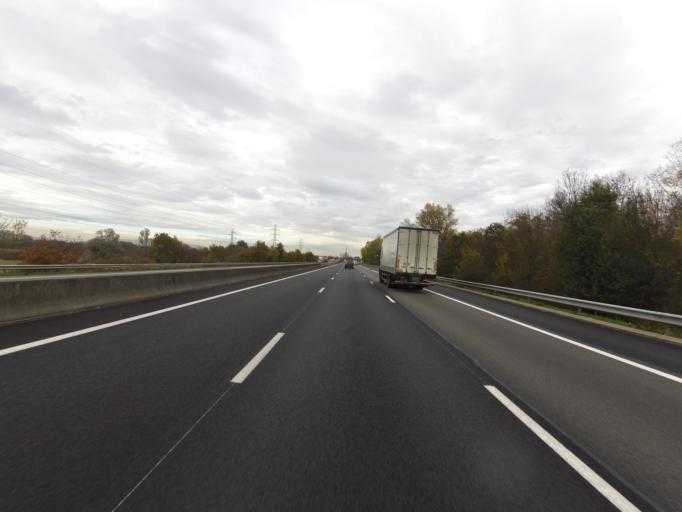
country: FR
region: Rhone-Alpes
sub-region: Departement du Rhone
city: Arnas
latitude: 46.0345
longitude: 4.7260
